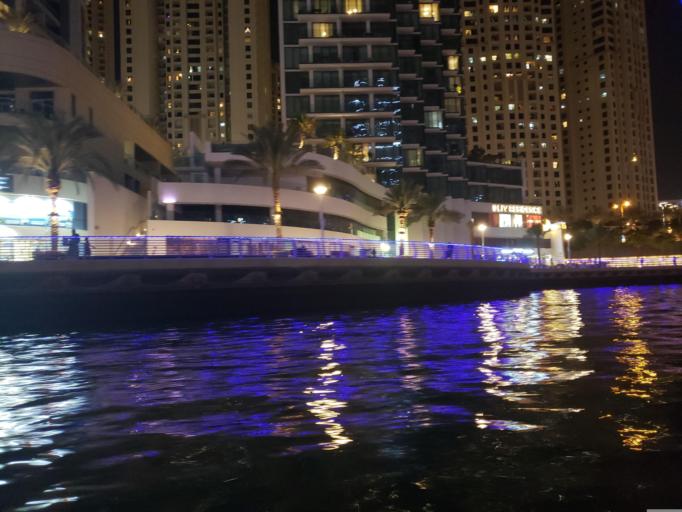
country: AE
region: Dubai
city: Dubai
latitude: 25.0804
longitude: 55.1413
